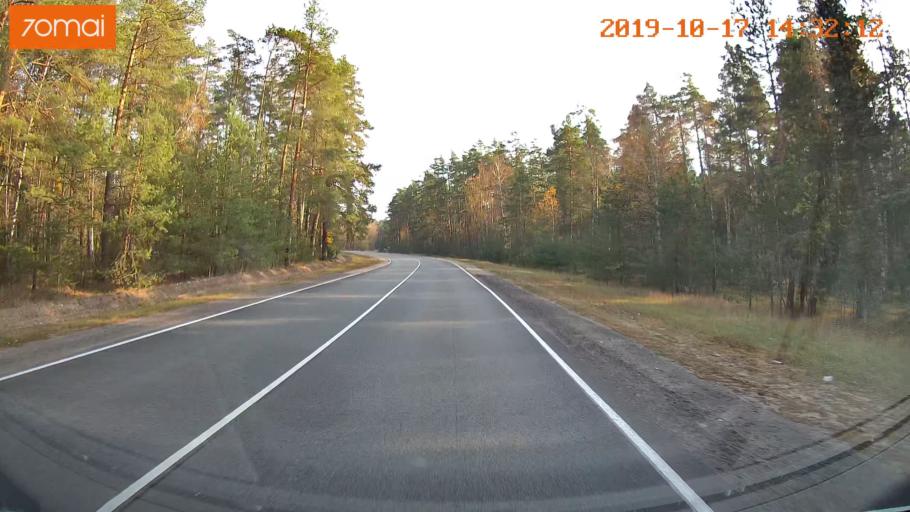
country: RU
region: Rjazan
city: Solotcha
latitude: 54.9297
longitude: 39.9754
